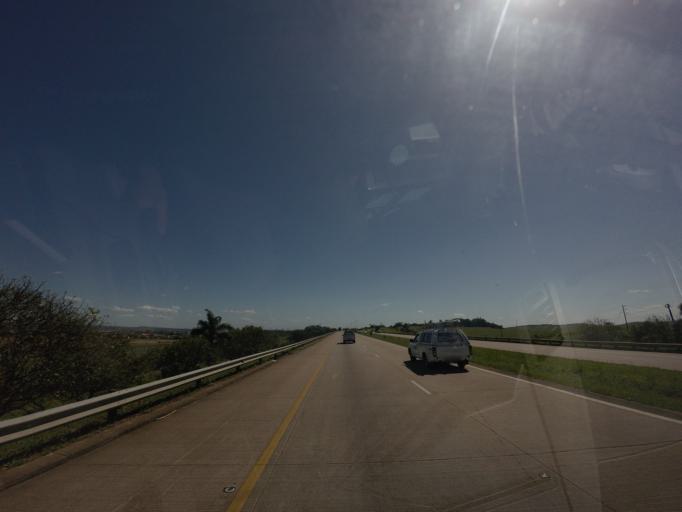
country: ZA
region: KwaZulu-Natal
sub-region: iLembe District Municipality
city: Stanger
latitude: -29.4134
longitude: 31.2787
